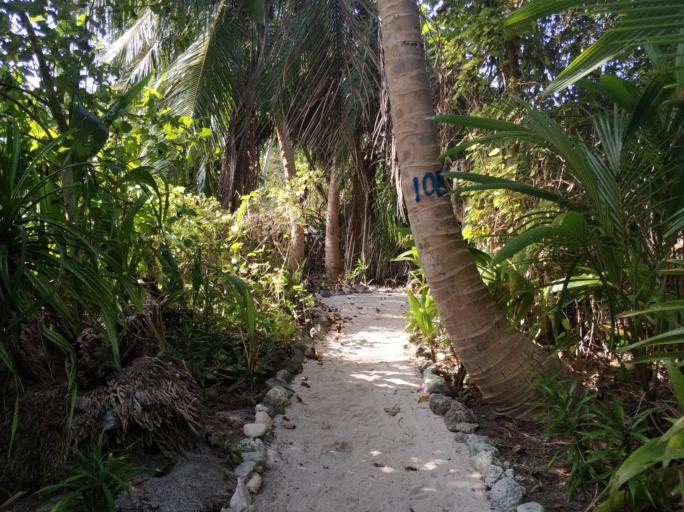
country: MV
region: Maale
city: Male
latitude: 4.4422
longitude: 72.9623
